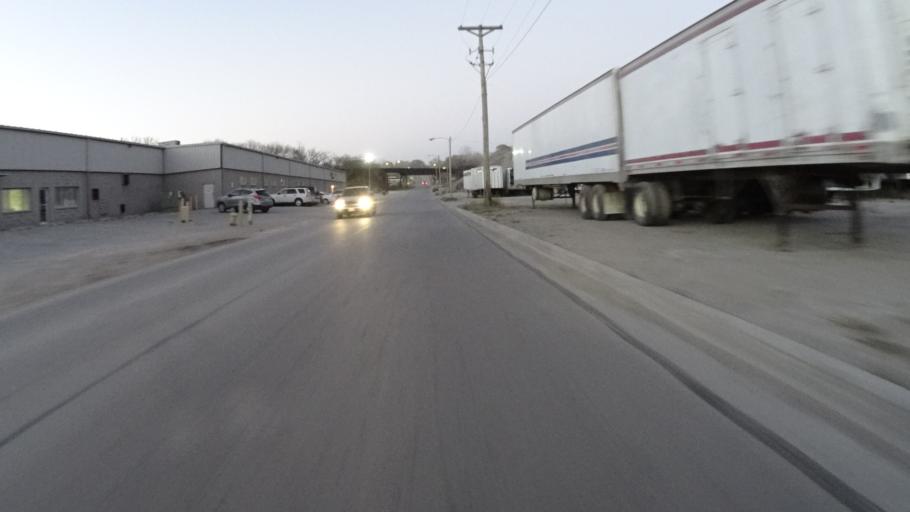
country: US
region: Nebraska
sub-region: Douglas County
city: Omaha
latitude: 41.2206
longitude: -95.9599
